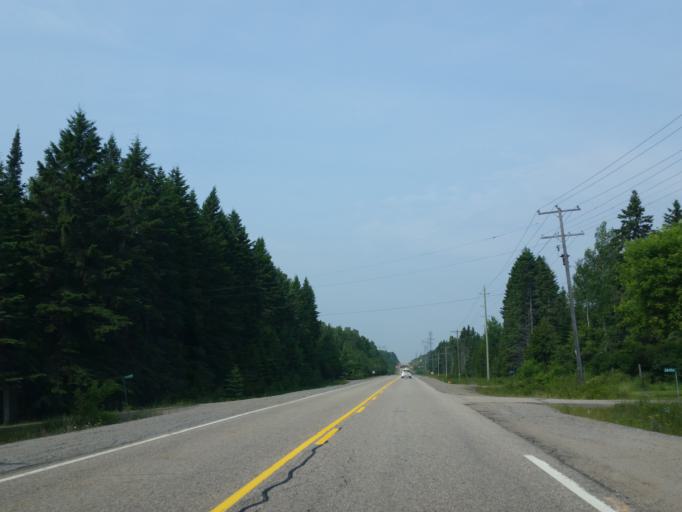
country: CA
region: Ontario
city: Bancroft
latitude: 45.5005
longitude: -78.1743
